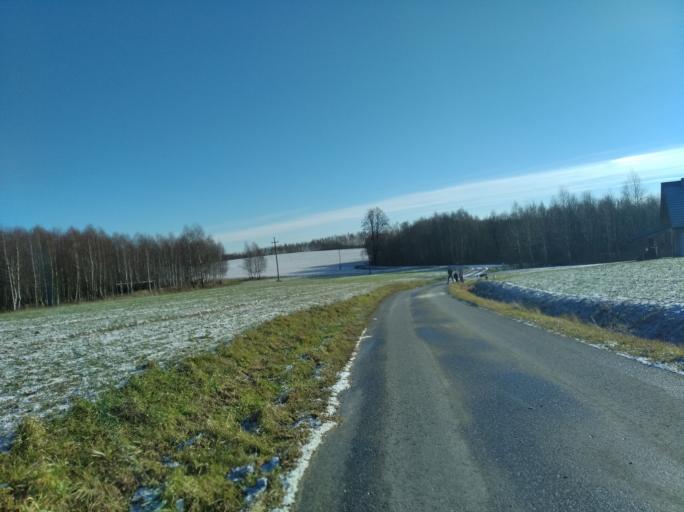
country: PL
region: Subcarpathian Voivodeship
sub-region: Powiat strzyzowski
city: Czudec
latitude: 49.9481
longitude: 21.7635
